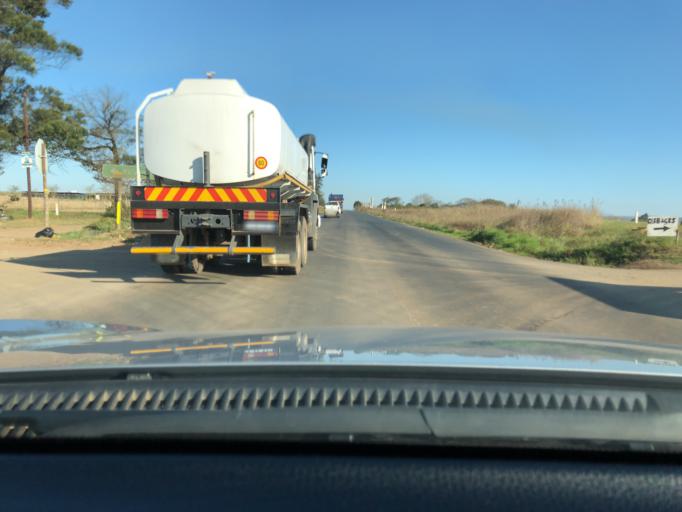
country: ZA
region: KwaZulu-Natal
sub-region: uMgungundlovu District Municipality
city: Camperdown
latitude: -29.7545
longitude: 30.5065
